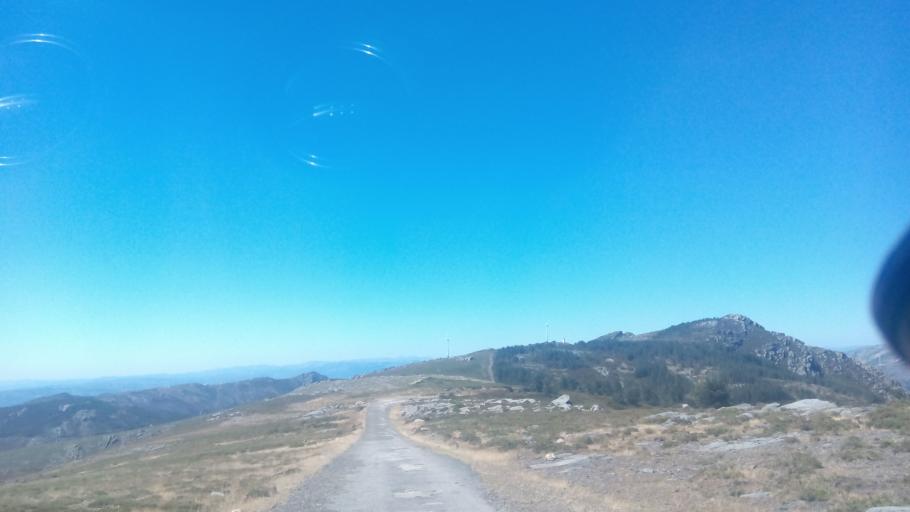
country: PT
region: Vila Real
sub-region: Mesao Frio
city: Mesao Frio
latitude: 41.2496
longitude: -7.8963
